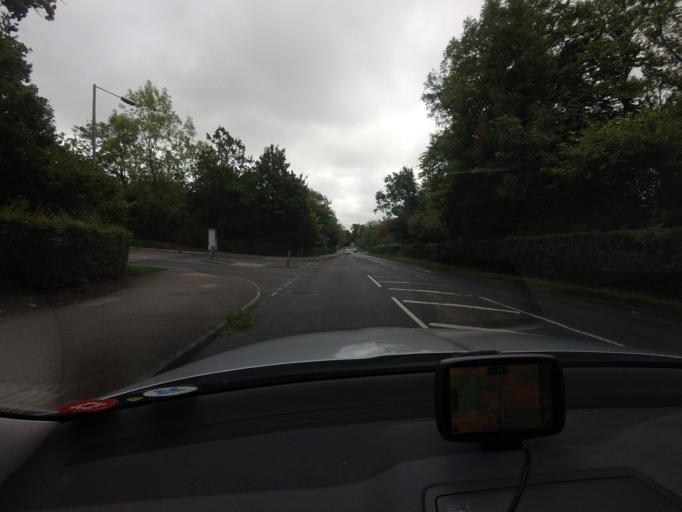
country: GB
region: England
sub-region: Kent
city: Tonbridge
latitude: 51.2141
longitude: 0.2475
